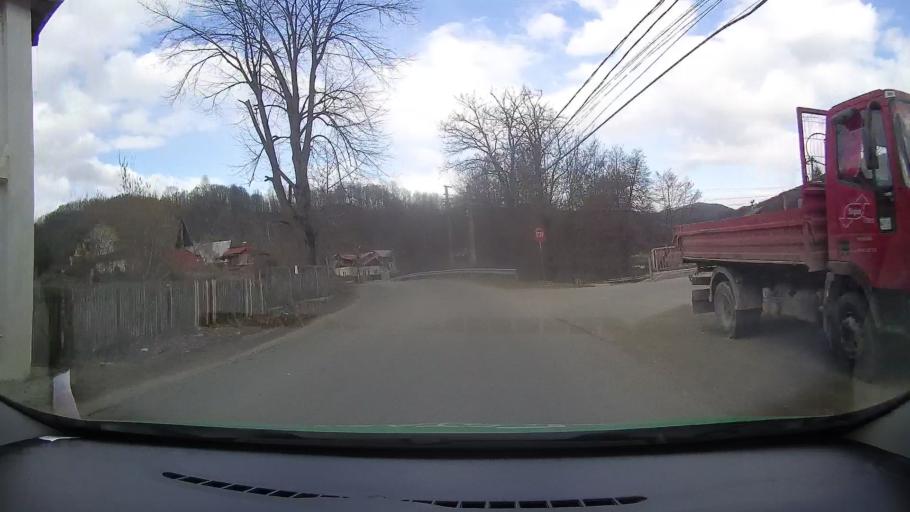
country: RO
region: Dambovita
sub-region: Comuna Visinesti
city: Visinesti
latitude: 45.0670
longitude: 25.5477
